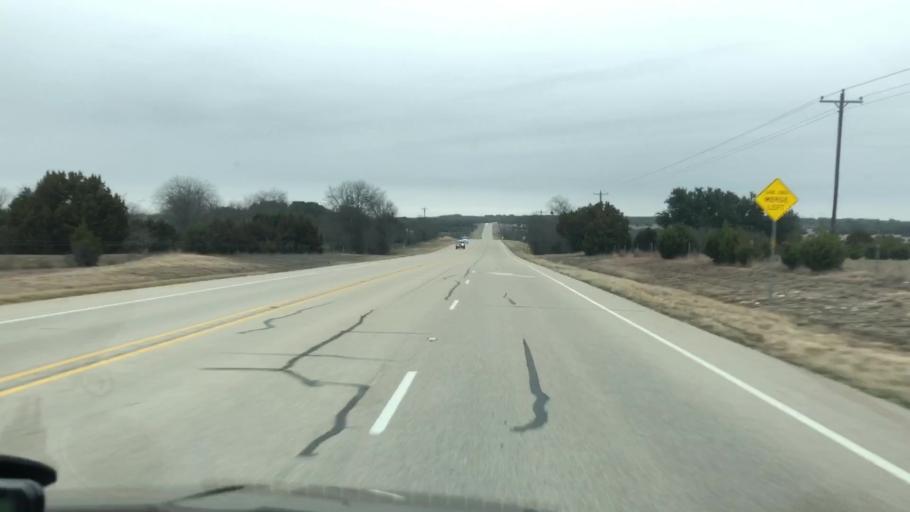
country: US
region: Texas
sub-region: Hamilton County
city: Hamilton
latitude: 31.8214
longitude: -98.1151
